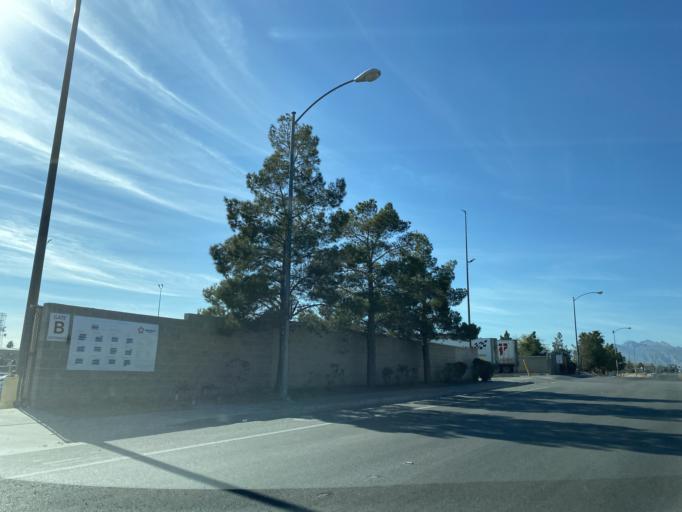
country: US
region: Nevada
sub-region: Clark County
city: North Las Vegas
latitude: 36.2249
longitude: -115.1450
